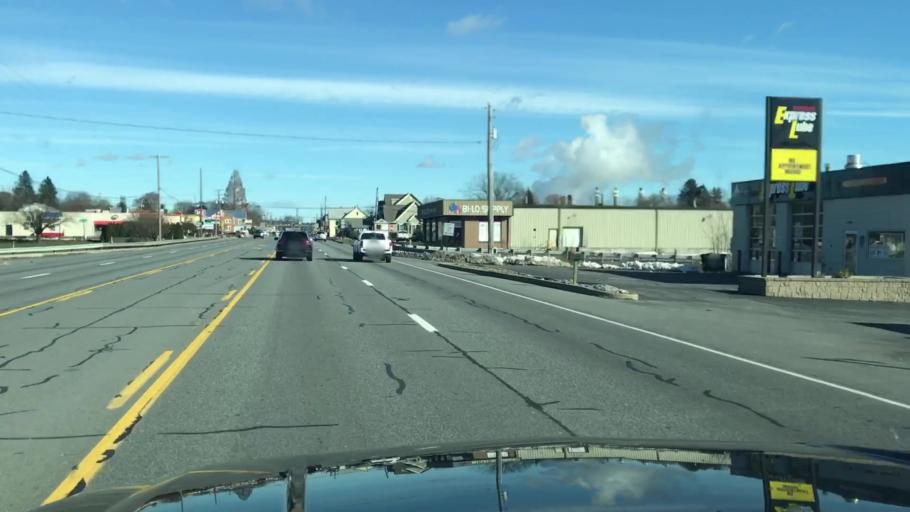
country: US
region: Pennsylvania
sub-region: Snyder County
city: Hummels Wharf
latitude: 40.8313
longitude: -76.8393
